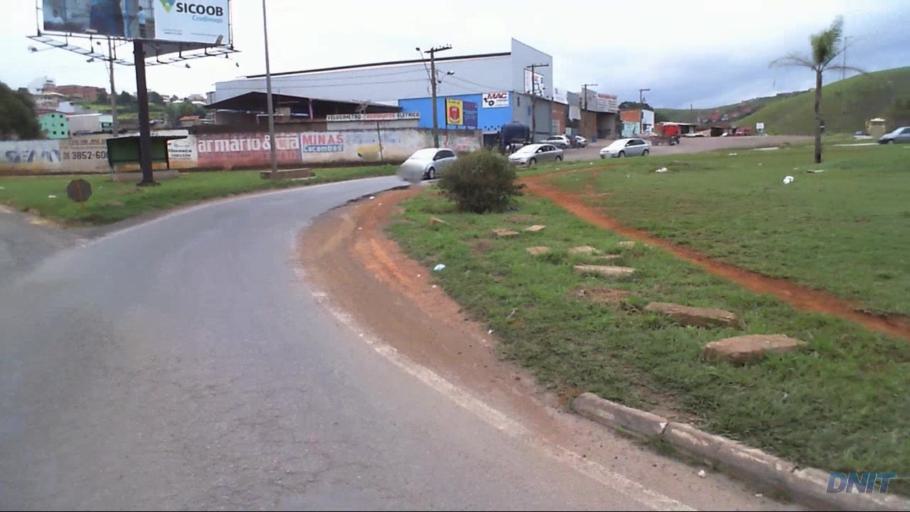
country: BR
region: Minas Gerais
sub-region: Joao Monlevade
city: Joao Monlevade
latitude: -19.8386
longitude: -43.1906
